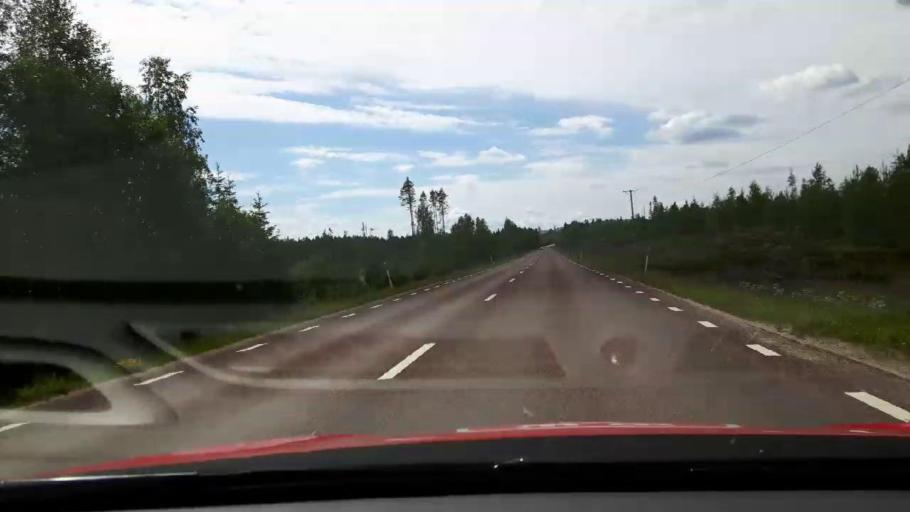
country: SE
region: Jaemtland
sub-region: Harjedalens Kommun
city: Sveg
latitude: 62.0590
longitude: 14.9097
